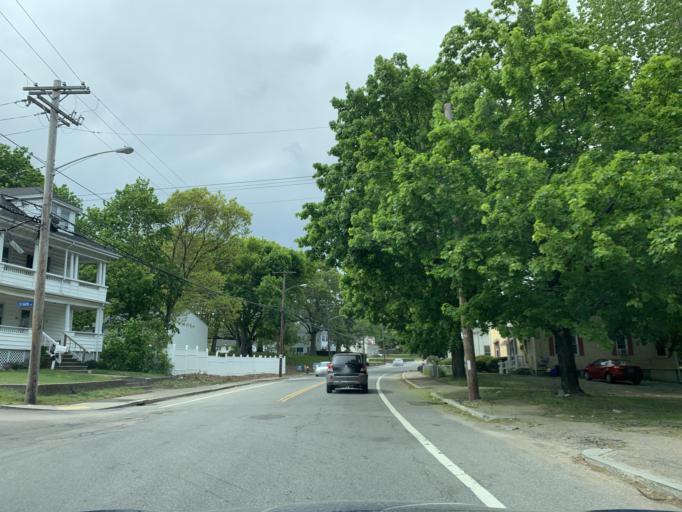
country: US
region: Rhode Island
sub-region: Providence County
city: Johnston
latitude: 41.7976
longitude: -71.4850
